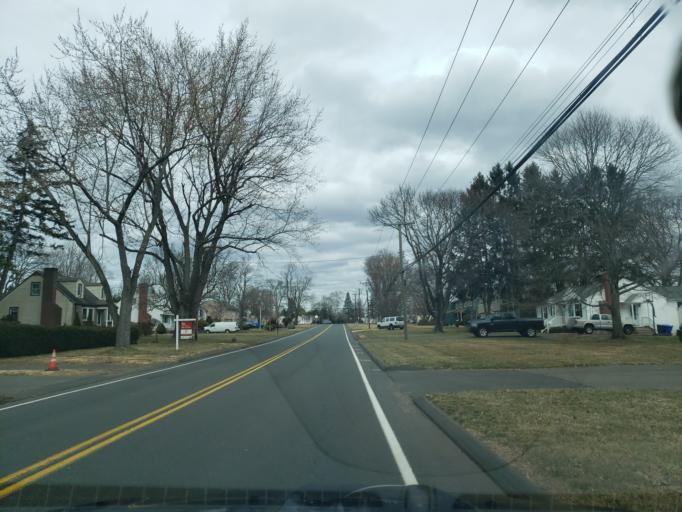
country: US
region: Connecticut
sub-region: Hartford County
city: Wethersfield
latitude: 41.6703
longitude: -72.6667
